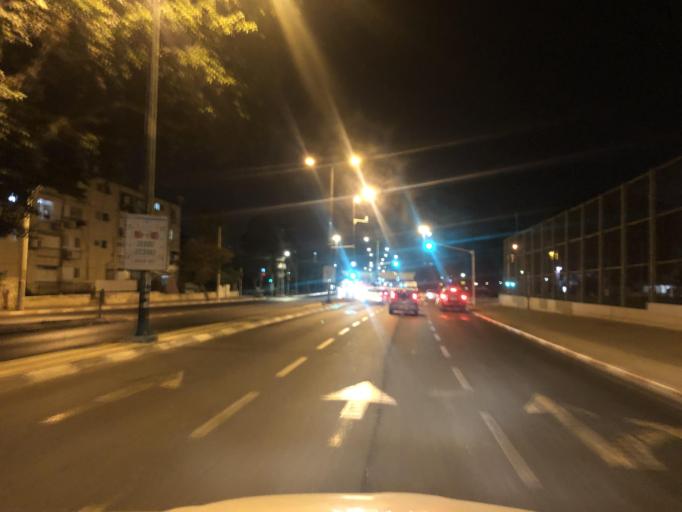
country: IL
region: Tel Aviv
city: Yafo
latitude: 32.0474
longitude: 34.7799
